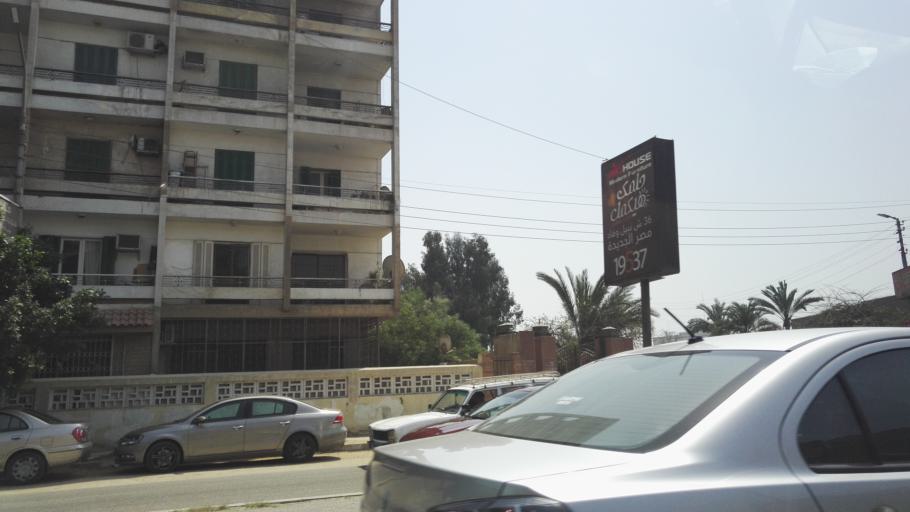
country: EG
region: Muhafazat al Qahirah
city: Cairo
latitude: 30.0807
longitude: 31.3309
